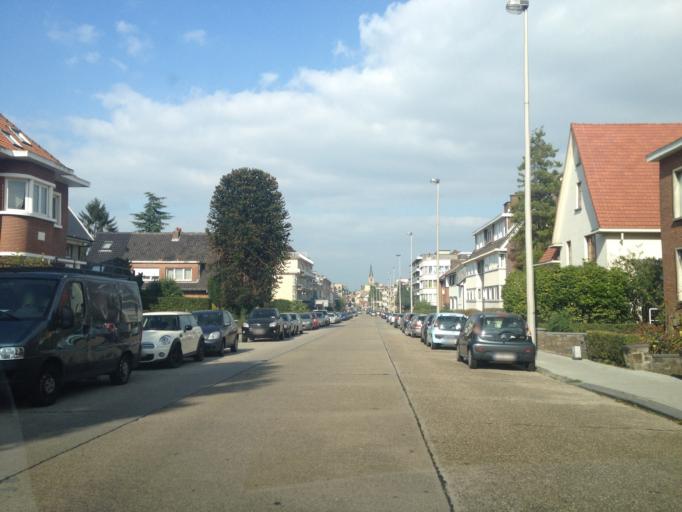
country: BE
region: Flanders
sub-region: Provincie Vlaams-Brabant
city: Bever
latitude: 50.9045
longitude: 4.3495
